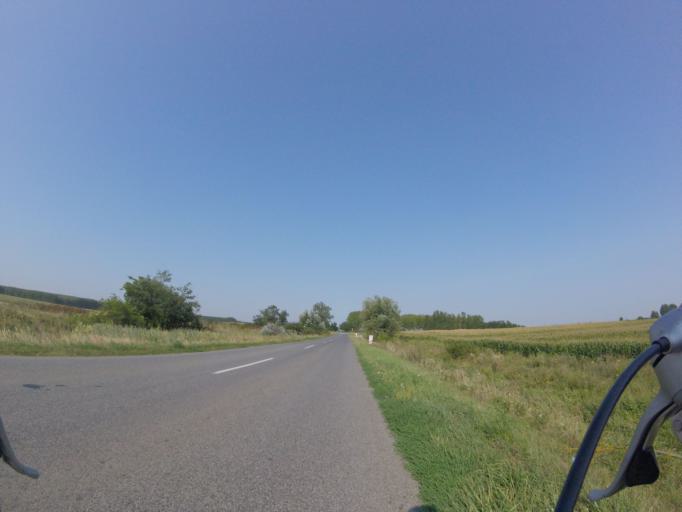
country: HU
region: Szabolcs-Szatmar-Bereg
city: Kotaj
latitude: 48.0549
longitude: 21.6851
